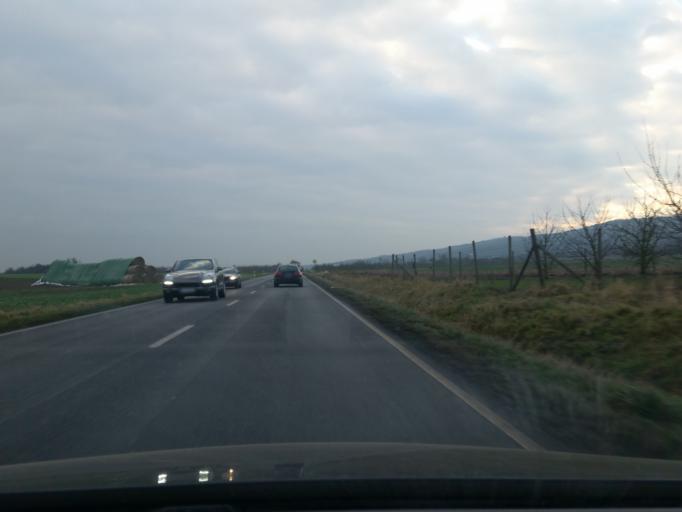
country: DE
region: Hesse
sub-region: Regierungsbezirk Darmstadt
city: Rosbach vor der Hohe
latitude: 50.3166
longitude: 8.7097
